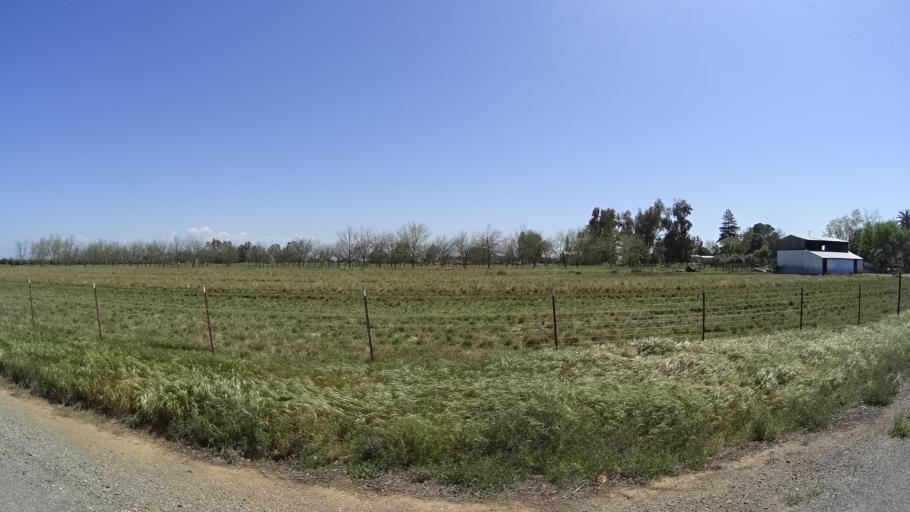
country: US
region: California
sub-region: Glenn County
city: Orland
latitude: 39.7707
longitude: -122.1830
